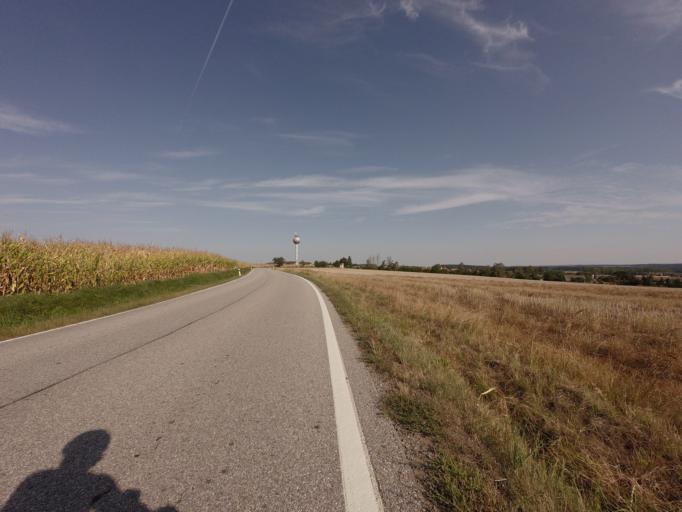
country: CZ
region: Jihocesky
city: Bernartice
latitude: 49.3009
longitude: 14.3838
